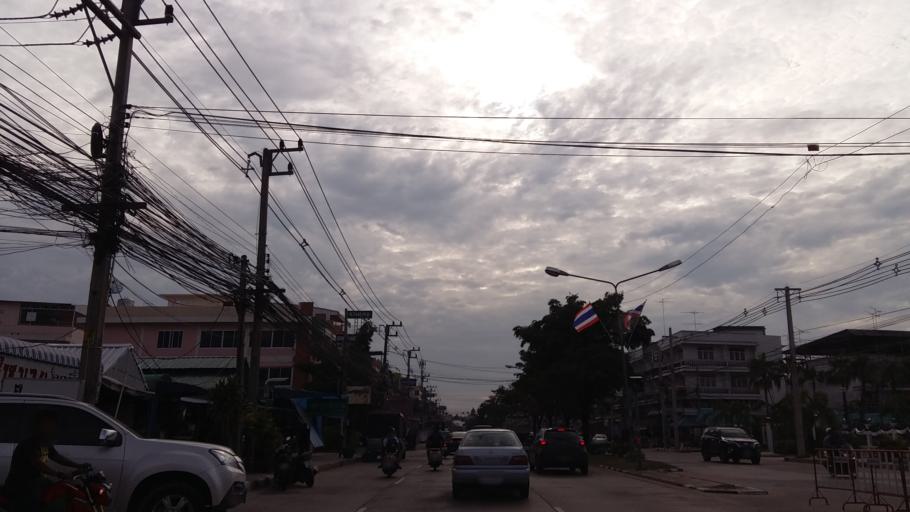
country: TH
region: Chon Buri
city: Chon Buri
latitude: 13.3467
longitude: 100.9704
